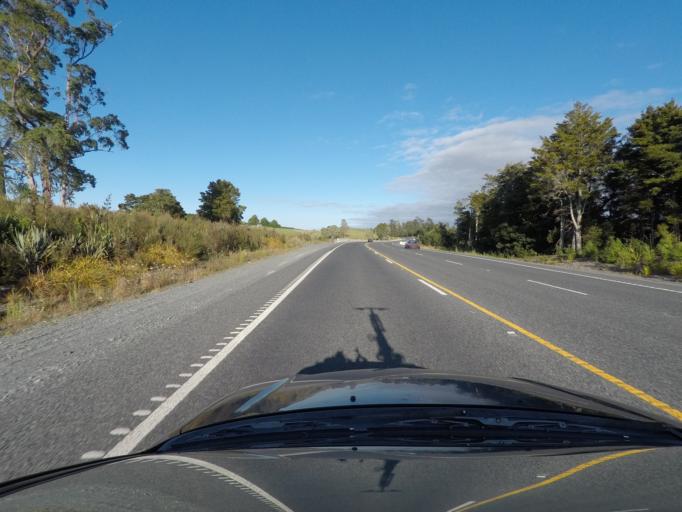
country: NZ
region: Northland
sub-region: Far North District
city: Kawakawa
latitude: -35.4980
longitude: 174.1650
